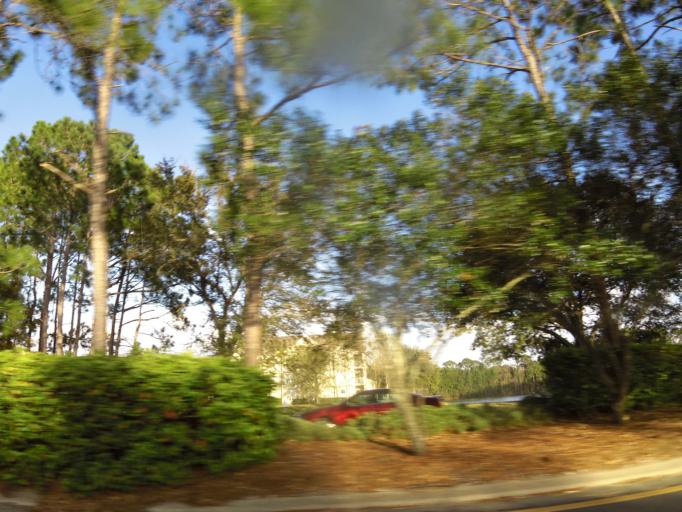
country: US
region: Florida
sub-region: Duval County
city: Jacksonville
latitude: 30.2655
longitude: -81.5504
